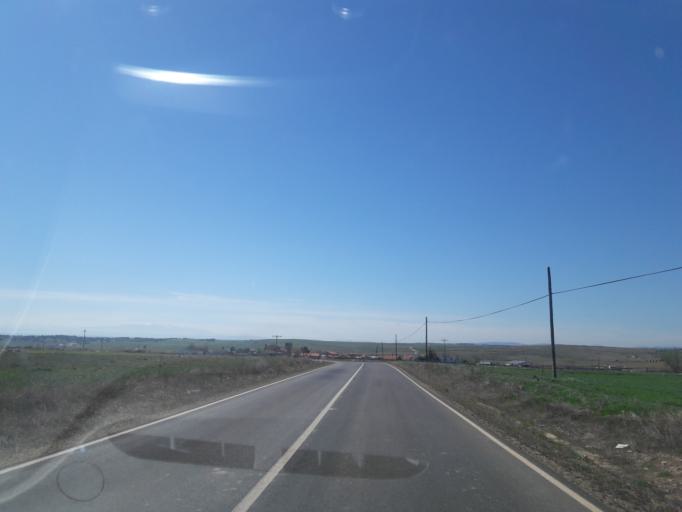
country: ES
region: Castille and Leon
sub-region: Provincia de Salamanca
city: Martinamor
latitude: 40.8105
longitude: -5.5964
